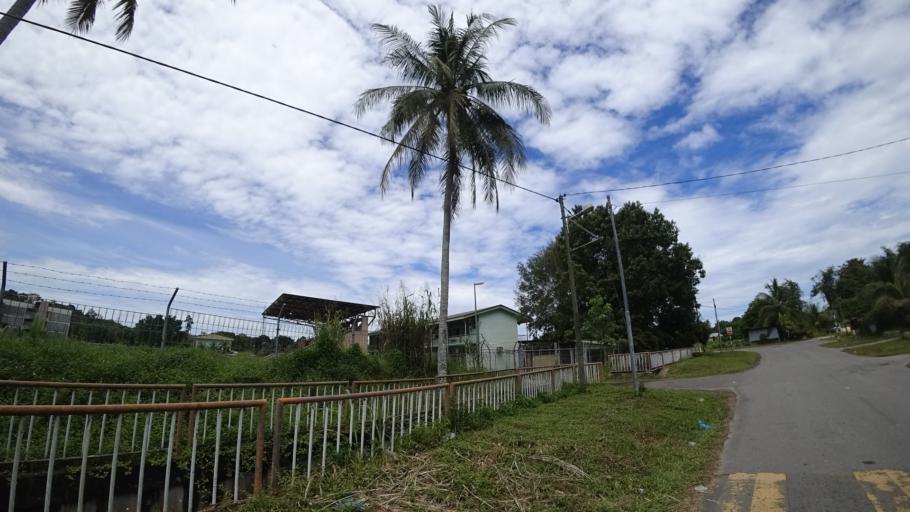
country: BN
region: Tutong
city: Tutong
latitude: 4.7705
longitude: 114.8188
